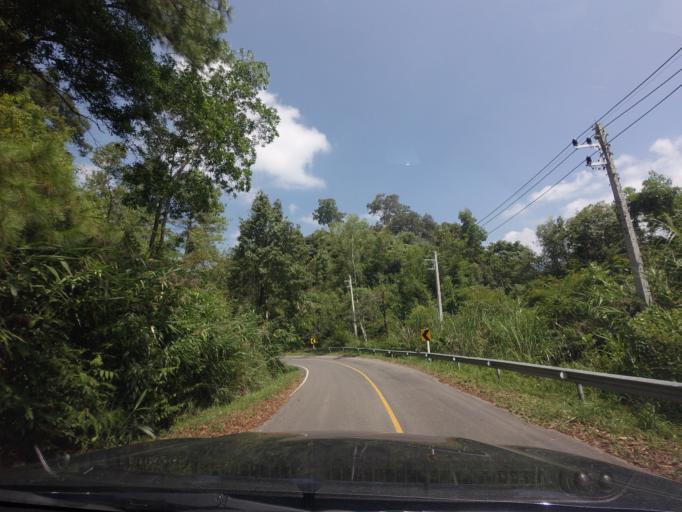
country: TH
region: Loei
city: Na Haeo
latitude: 17.4925
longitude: 100.9009
